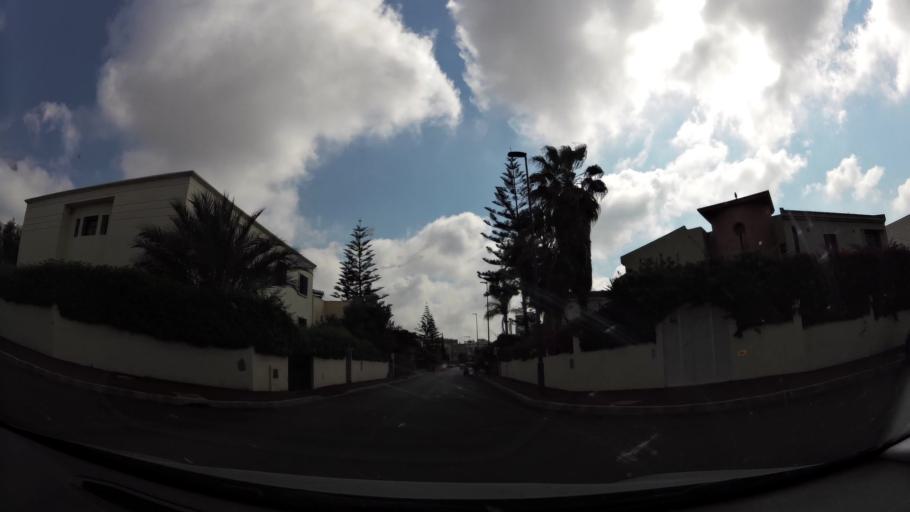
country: MA
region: Rabat-Sale-Zemmour-Zaer
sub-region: Skhirate-Temara
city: Temara
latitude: 33.9579
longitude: -6.8627
